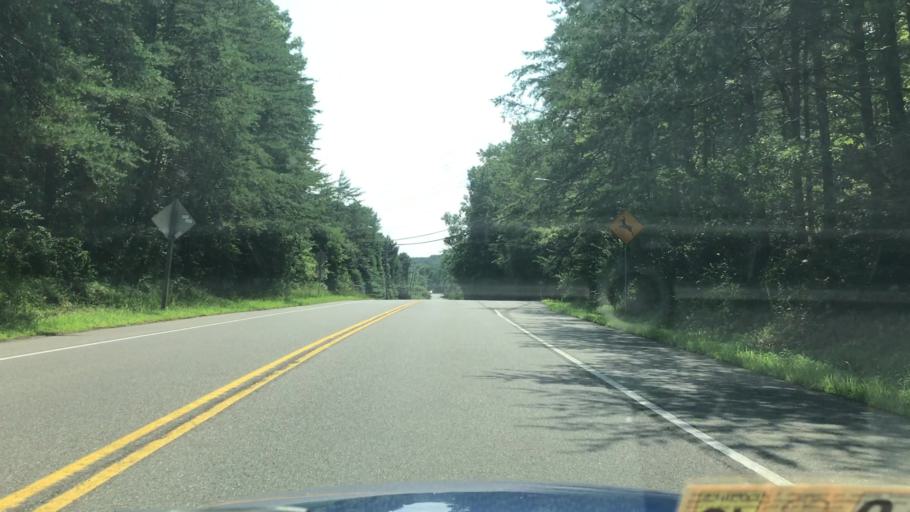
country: US
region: Virginia
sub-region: Fairfax County
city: Wolf Trap
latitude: 38.9270
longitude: -77.3221
